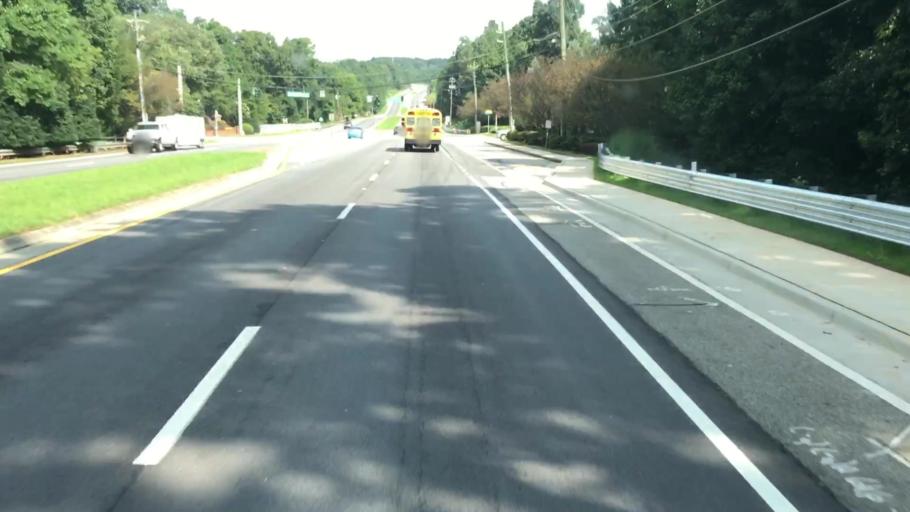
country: US
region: Georgia
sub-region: Gwinnett County
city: Lawrenceville
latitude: 33.9275
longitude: -84.0247
